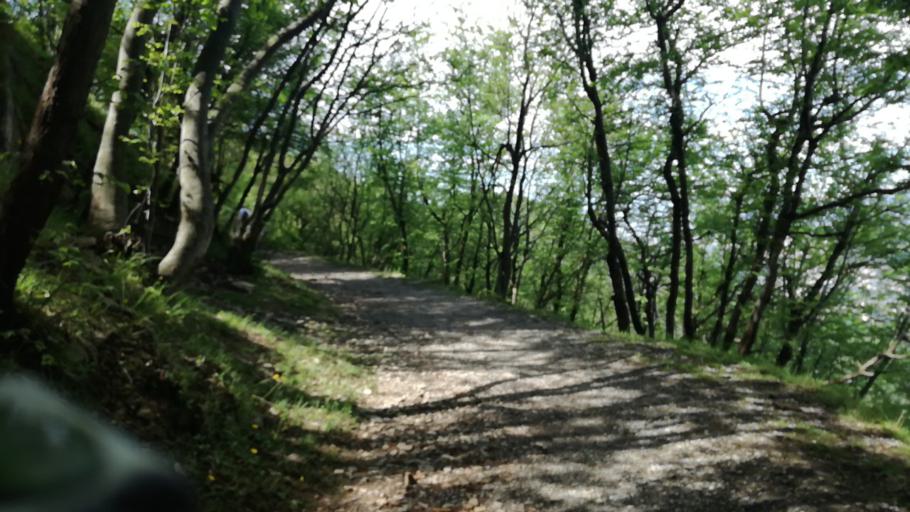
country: IT
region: Liguria
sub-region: Provincia di Genova
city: Genoa
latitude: 44.4448
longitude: 8.9349
